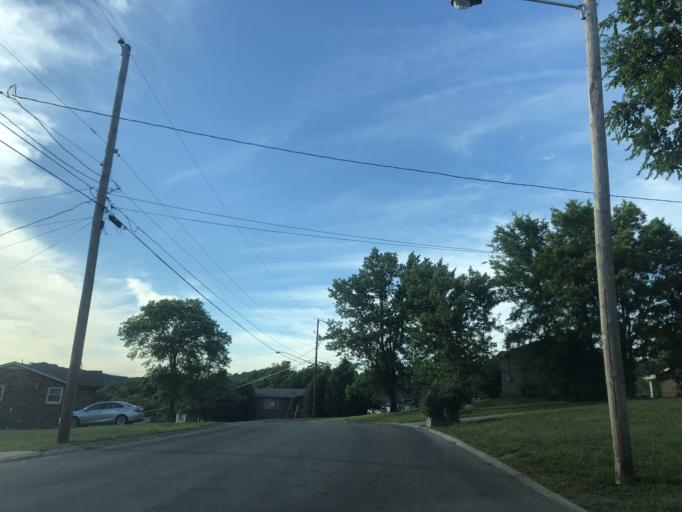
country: US
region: Tennessee
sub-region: Davidson County
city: Nashville
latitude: 36.2206
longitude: -86.8469
